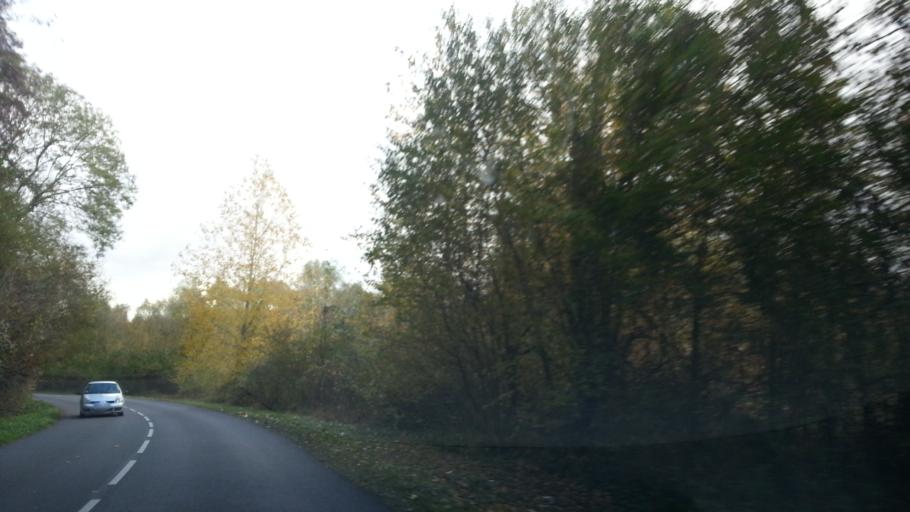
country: FR
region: Picardie
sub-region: Departement de l'Oise
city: Cires-les-Mello
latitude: 49.2655
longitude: 2.3723
